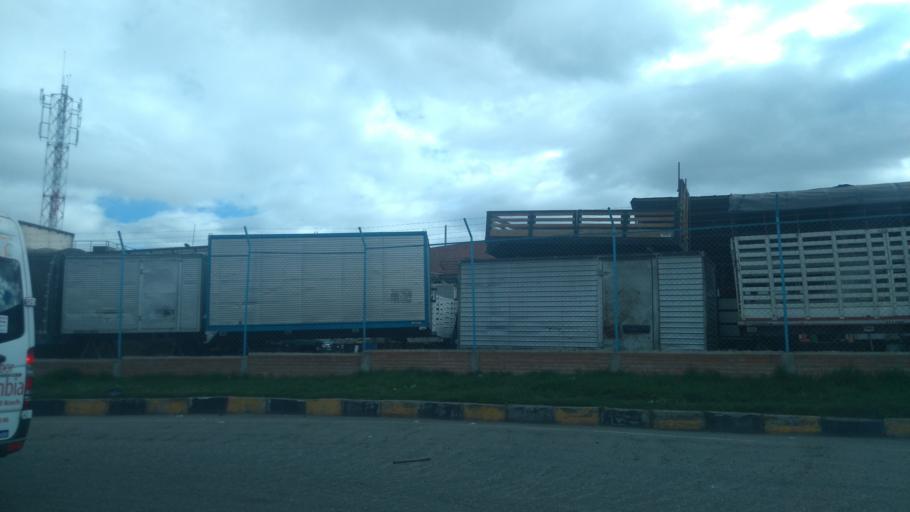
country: CO
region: Bogota D.C.
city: Bogota
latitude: 4.6459
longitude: -74.1323
